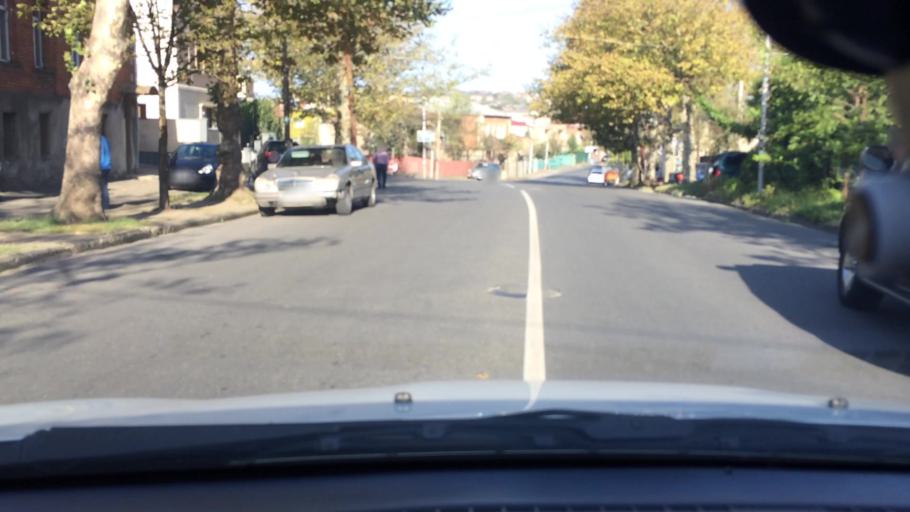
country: GE
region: Imereti
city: Kutaisi
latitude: 42.2689
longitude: 42.7153
